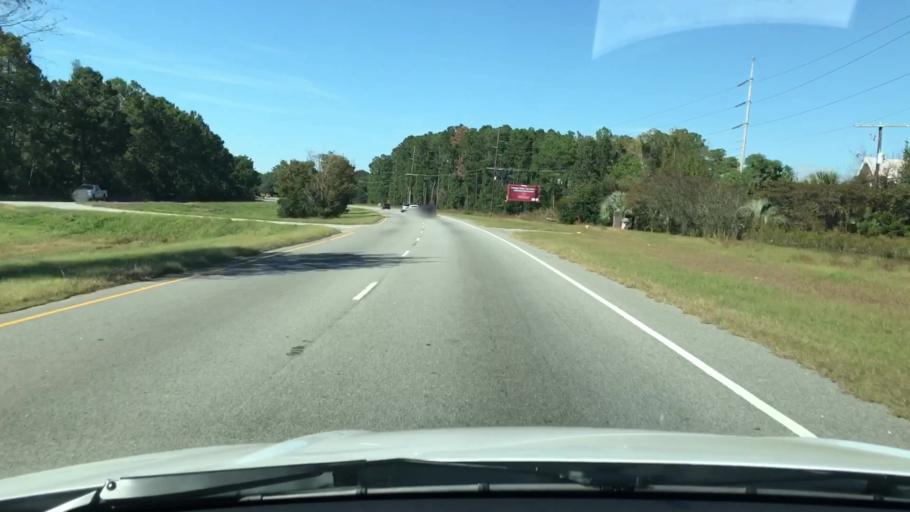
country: US
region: South Carolina
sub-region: Beaufort County
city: Laurel Bay
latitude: 32.5070
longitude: -80.7457
